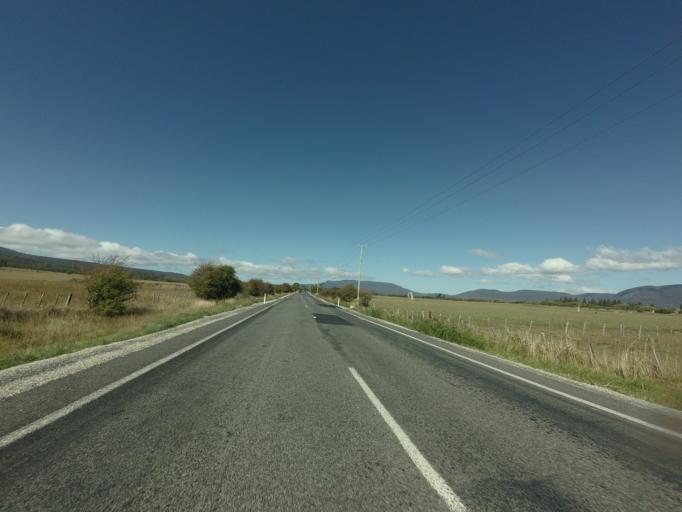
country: AU
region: Tasmania
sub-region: Break O'Day
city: St Helens
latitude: -41.5769
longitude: 148.1277
